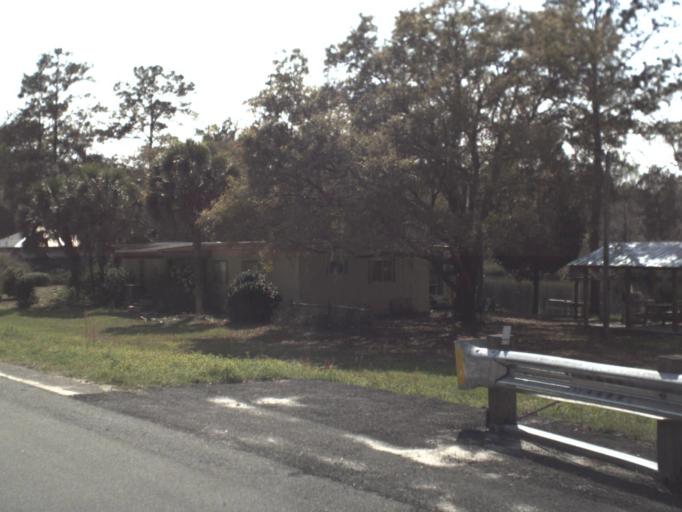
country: US
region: Florida
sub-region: Wakulla County
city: Crawfordville
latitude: 30.0215
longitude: -84.4999
